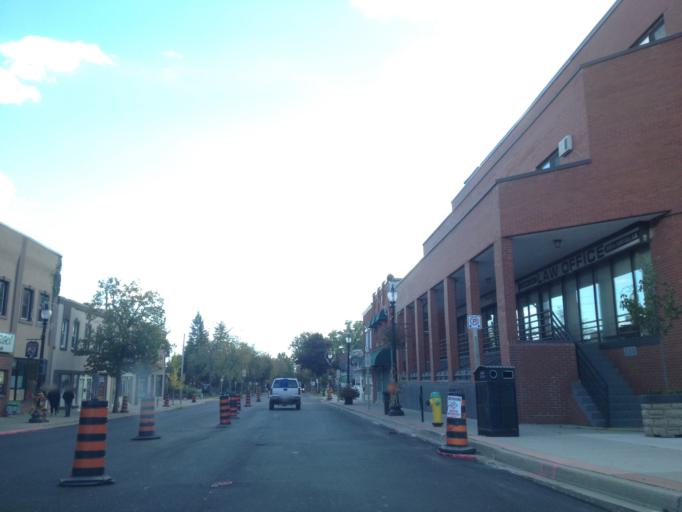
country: CA
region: Ontario
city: Amherstburg
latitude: 42.0378
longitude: -82.7397
